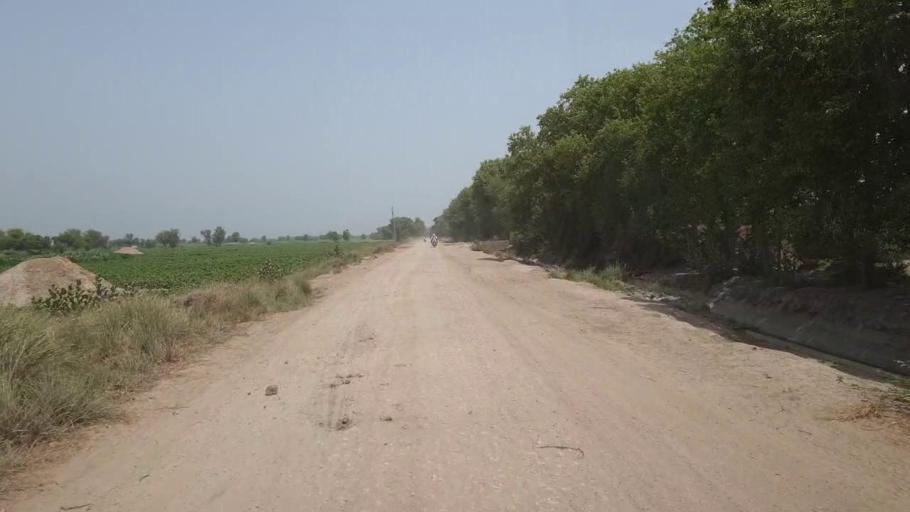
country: PK
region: Sindh
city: Nawabshah
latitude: 26.3230
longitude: 68.2971
